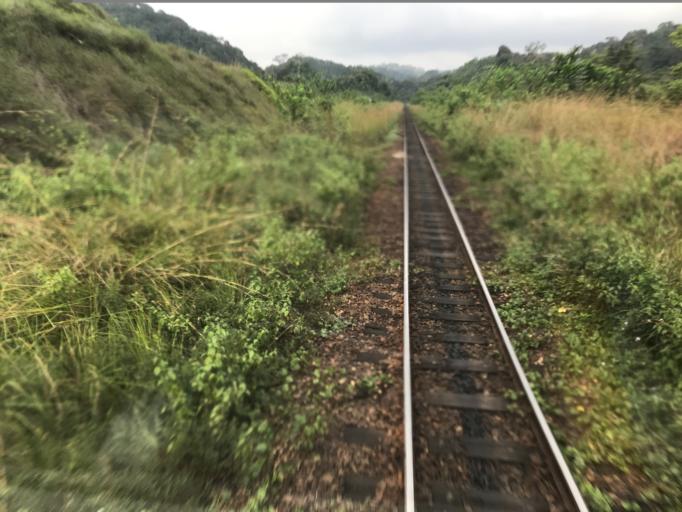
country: CM
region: Centre
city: Eseka
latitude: 3.5897
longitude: 10.8336
